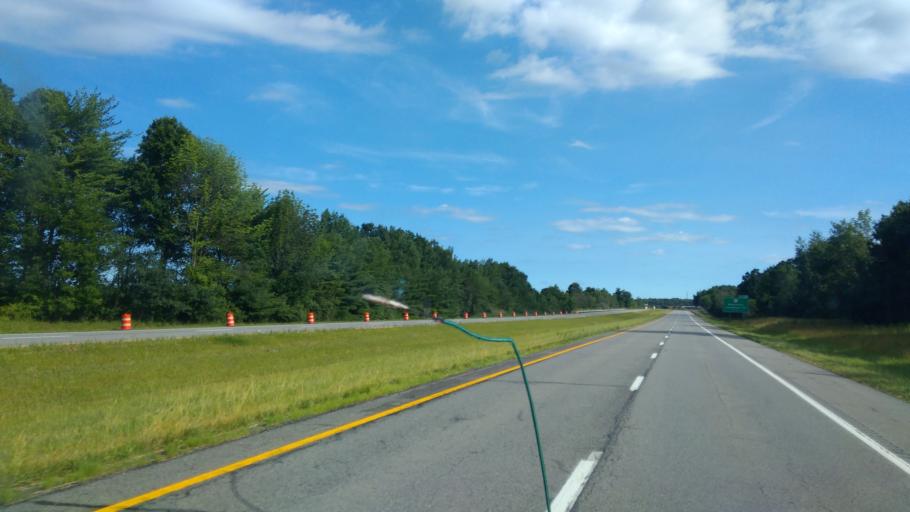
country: US
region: Ohio
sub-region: Trumbull County
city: Cortland
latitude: 41.4504
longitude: -80.7129
